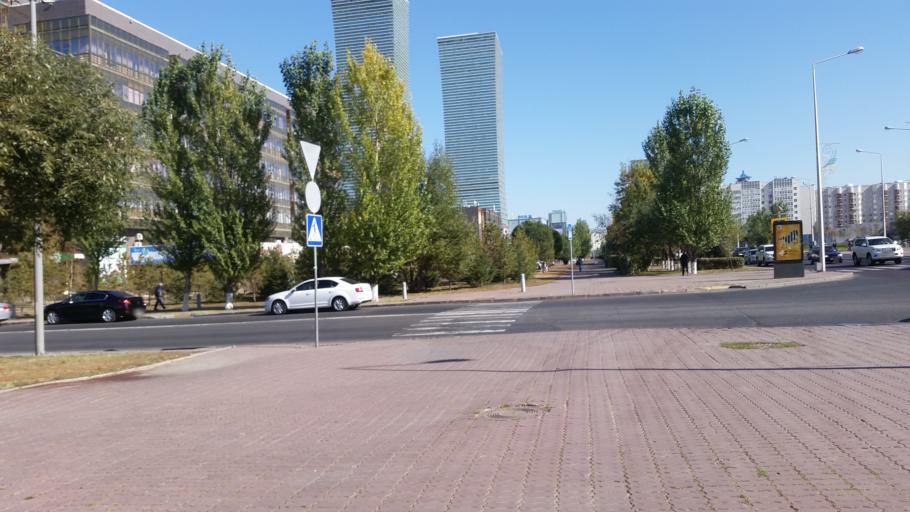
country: KZ
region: Astana Qalasy
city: Astana
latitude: 51.1282
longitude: 71.4163
